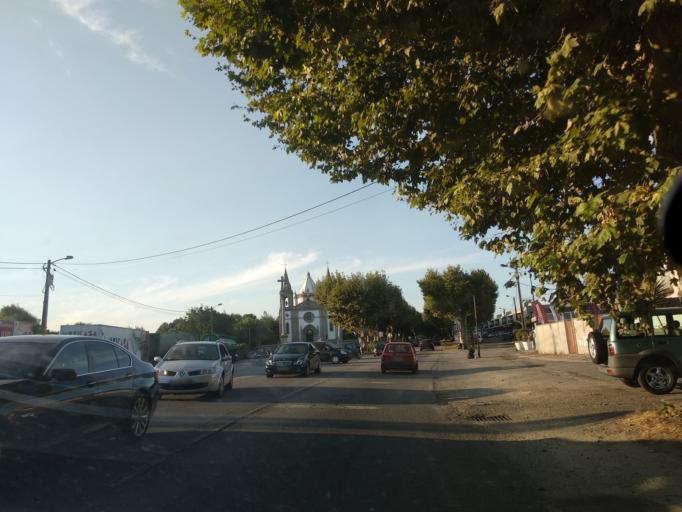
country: PT
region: Braga
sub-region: Vila Verde
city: Vila Verde
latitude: 41.6246
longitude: -8.4335
